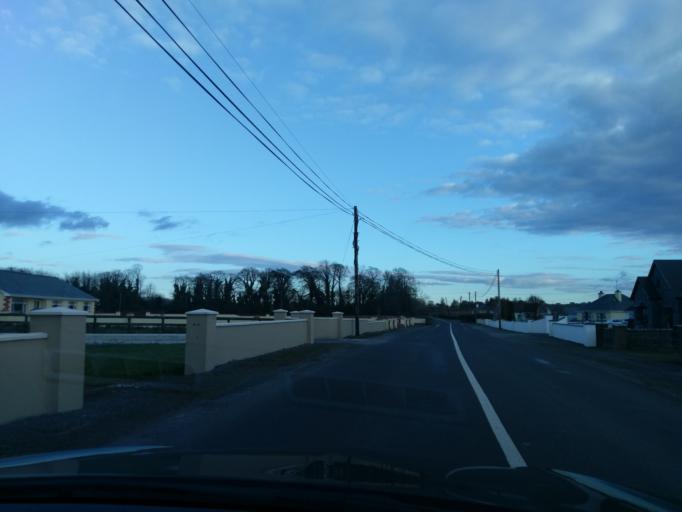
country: IE
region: Connaught
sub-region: County Galway
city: Athenry
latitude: 53.4360
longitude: -8.7160
